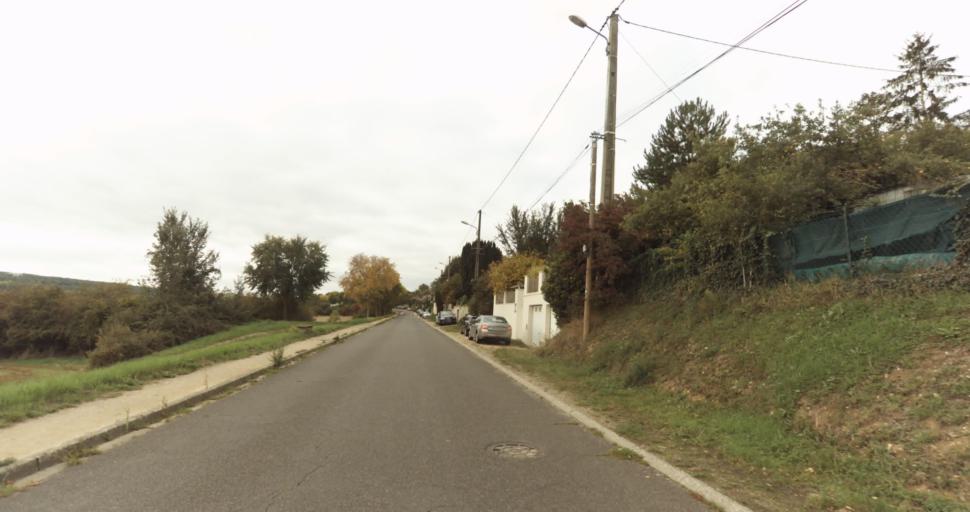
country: FR
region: Centre
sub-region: Departement d'Eure-et-Loir
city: Dreux
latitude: 48.7270
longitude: 1.3511
